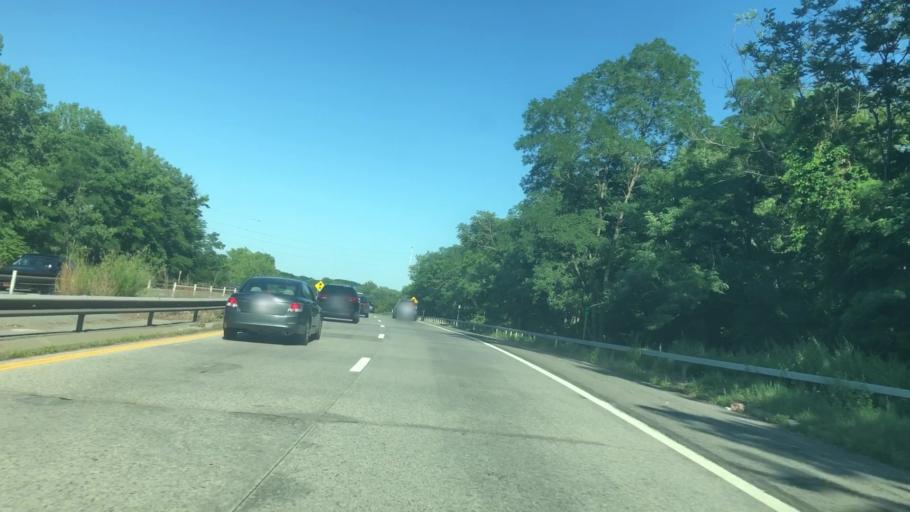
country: US
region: New York
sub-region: Monroe County
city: East Rochester
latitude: 43.1233
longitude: -77.5145
